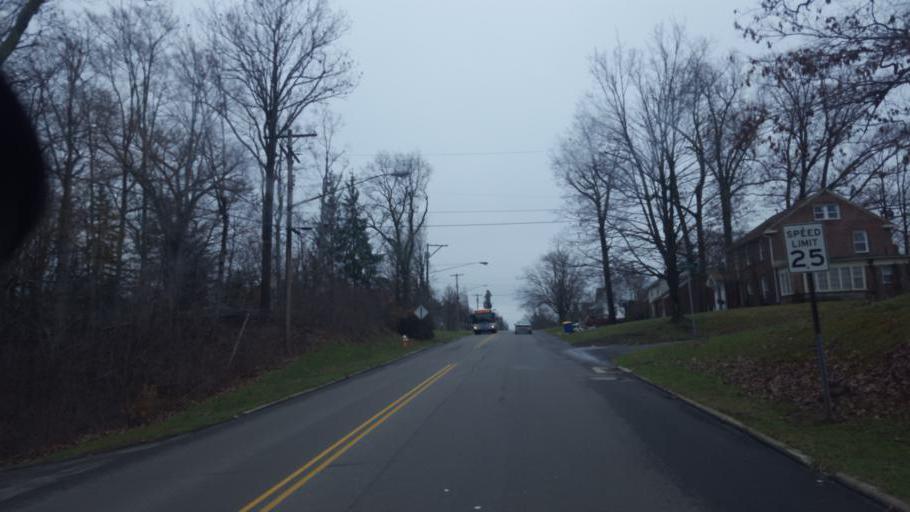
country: US
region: Ohio
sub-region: Richland County
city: Mansfield
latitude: 40.7545
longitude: -82.5467
